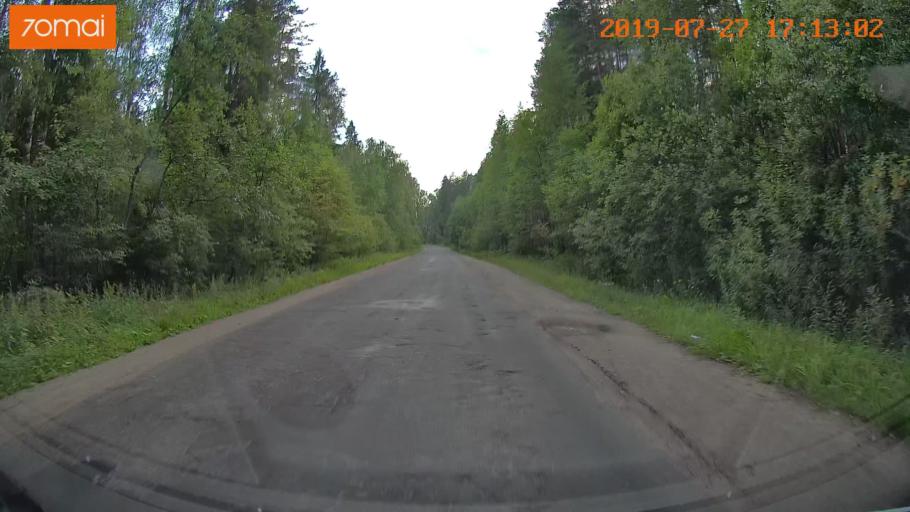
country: RU
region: Ivanovo
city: Novo-Talitsy
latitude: 57.0542
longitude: 40.8563
